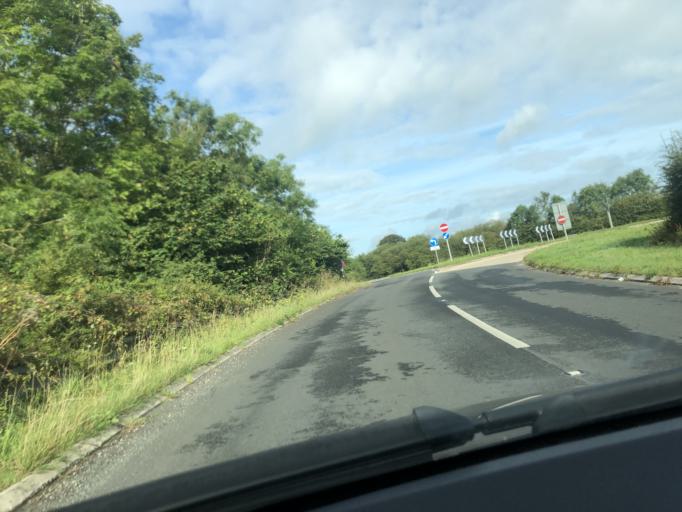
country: GB
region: England
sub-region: Cornwall
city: Launceston
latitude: 50.6447
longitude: -4.3024
